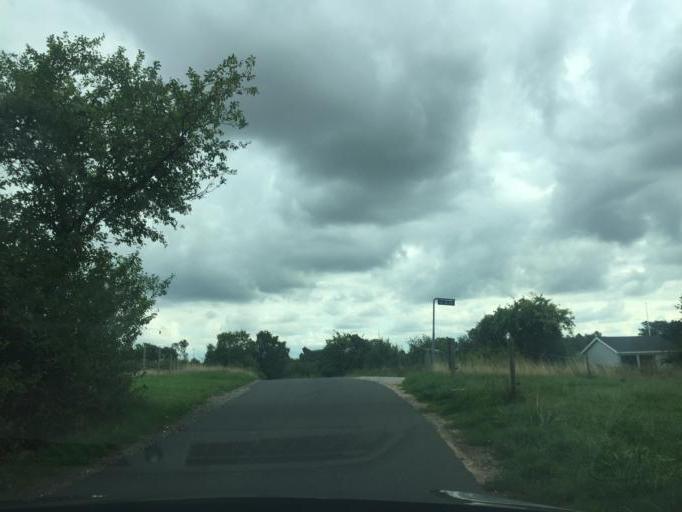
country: DK
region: South Denmark
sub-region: Assens Kommune
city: Tommerup
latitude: 55.3567
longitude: 10.2260
